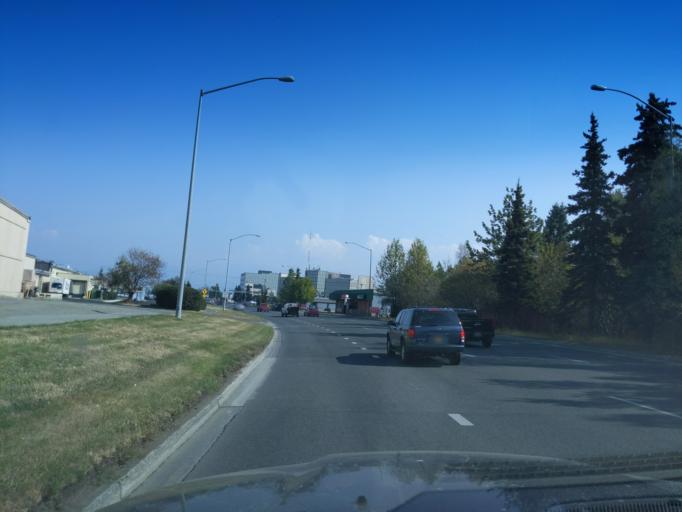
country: US
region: Alaska
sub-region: Anchorage Municipality
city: Anchorage
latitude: 61.1938
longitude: -149.9174
